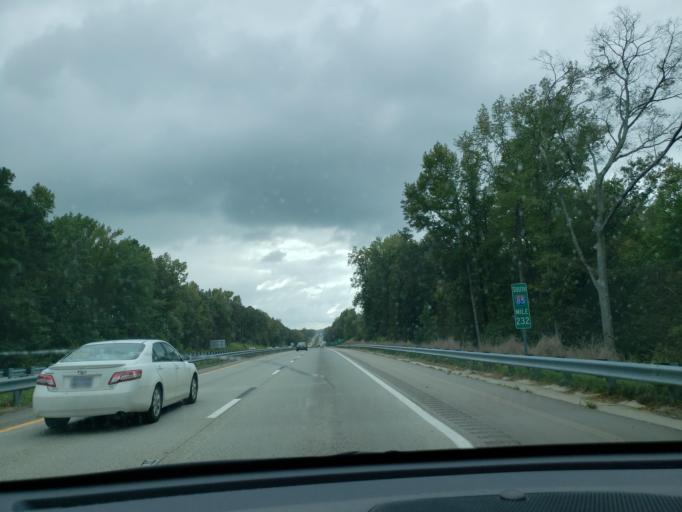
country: US
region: North Carolina
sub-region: Warren County
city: Norlina
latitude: 36.5256
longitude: -78.1979
